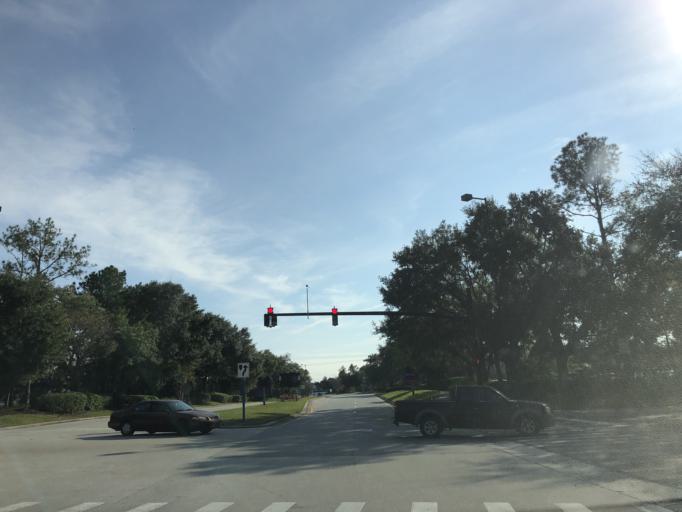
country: US
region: Florida
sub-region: Osceola County
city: Celebration
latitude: 28.3661
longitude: -81.5537
